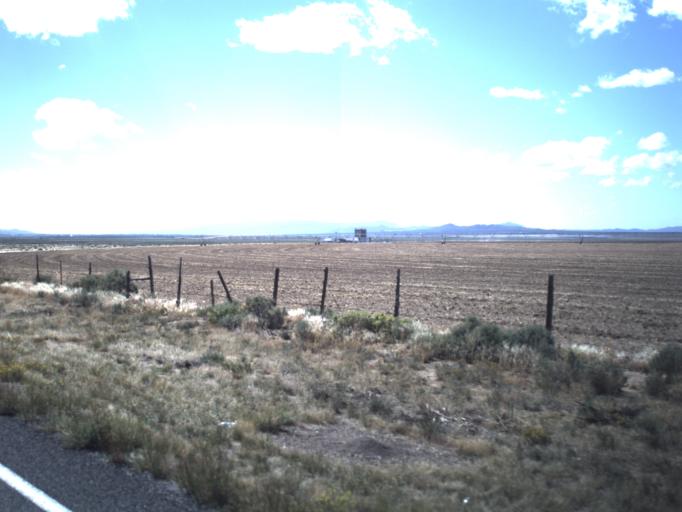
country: US
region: Utah
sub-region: Iron County
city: Enoch
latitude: 37.8939
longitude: -113.0316
